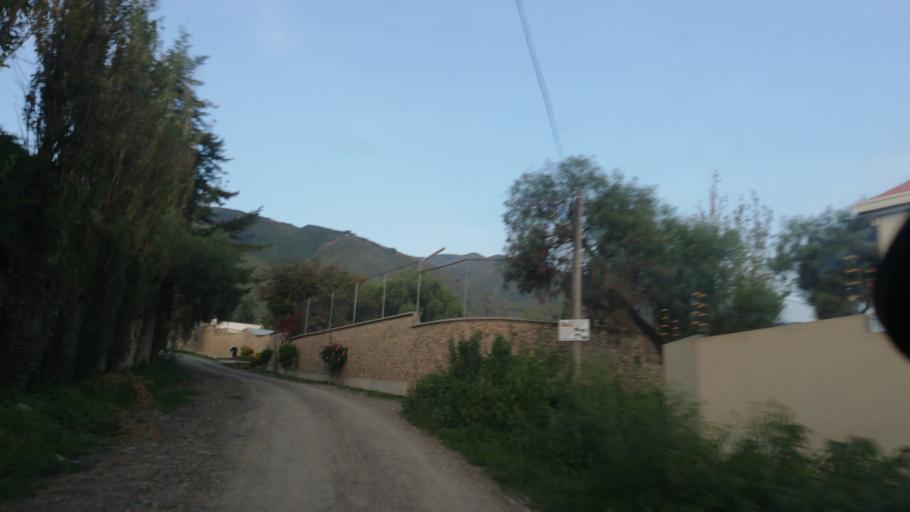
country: BO
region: Cochabamba
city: Cochabamba
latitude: -17.3340
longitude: -66.2087
